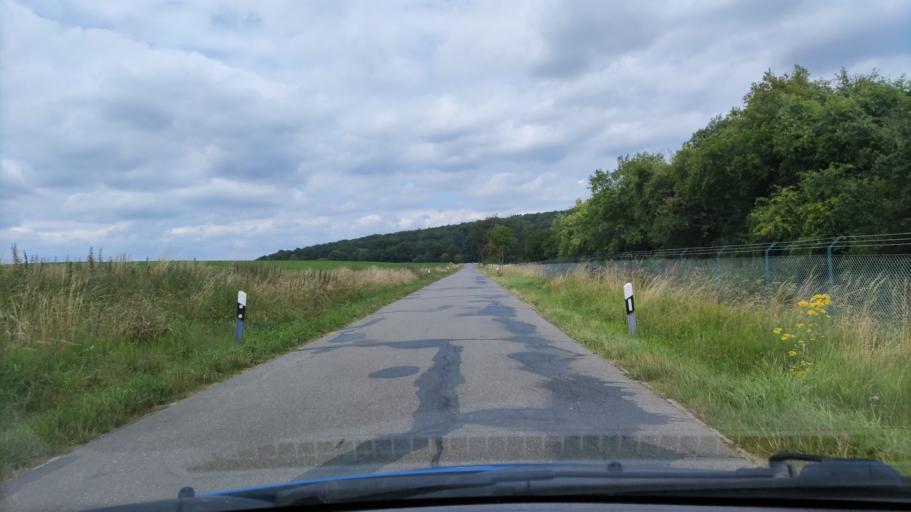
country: DE
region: Lower Saxony
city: Weste
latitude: 53.0754
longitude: 10.6895
